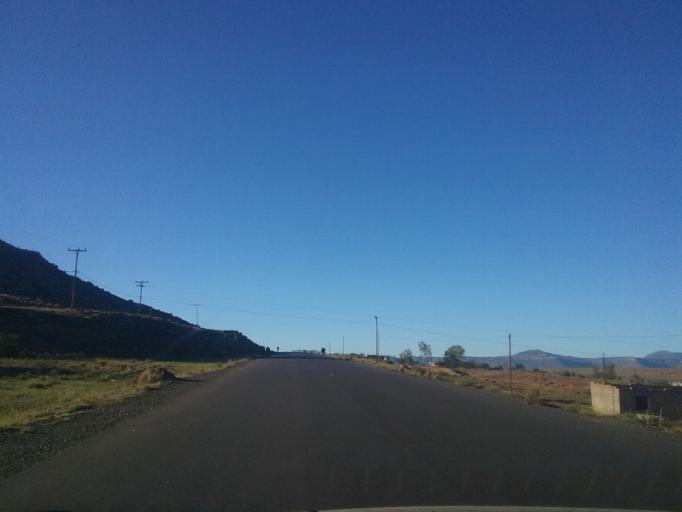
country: LS
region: Quthing
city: Quthing
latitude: -30.3468
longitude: 27.5428
